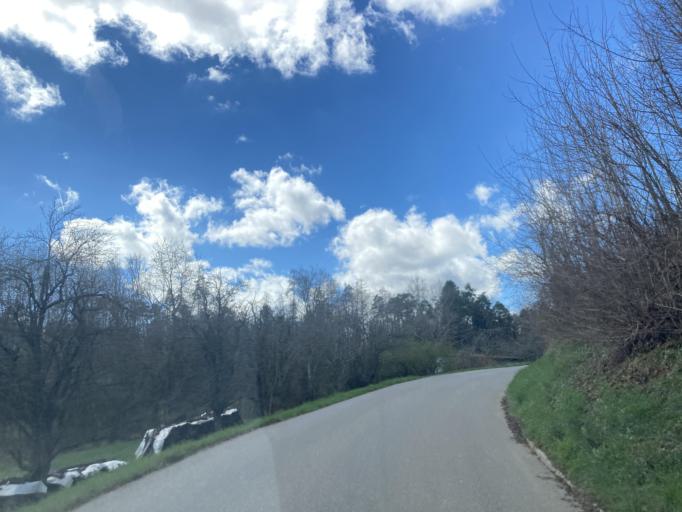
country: DE
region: Baden-Wuerttemberg
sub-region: Tuebingen Region
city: Hirrlingen
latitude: 48.4547
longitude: 8.8492
